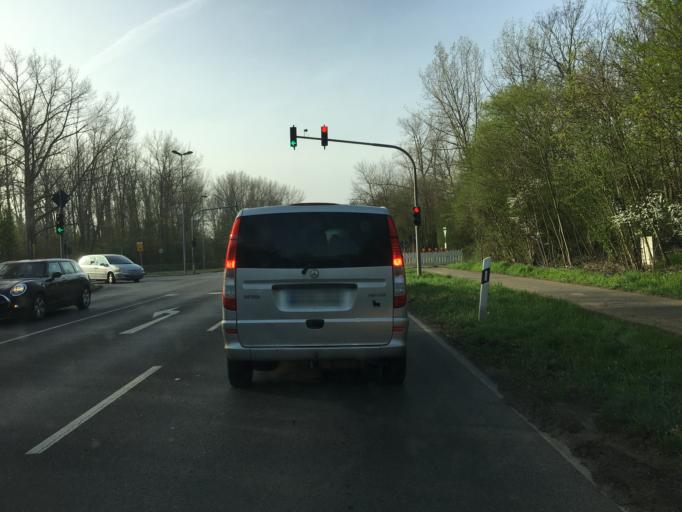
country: DE
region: North Rhine-Westphalia
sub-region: Regierungsbezirk Koln
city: Hurth
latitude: 50.8797
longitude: 6.8657
